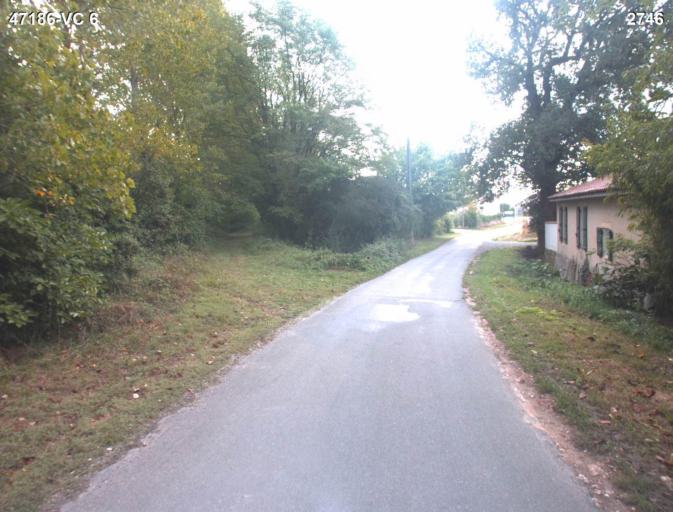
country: FR
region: Aquitaine
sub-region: Departement du Lot-et-Garonne
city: Sainte-Colombe-en-Bruilhois
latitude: 44.2175
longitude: 0.4654
